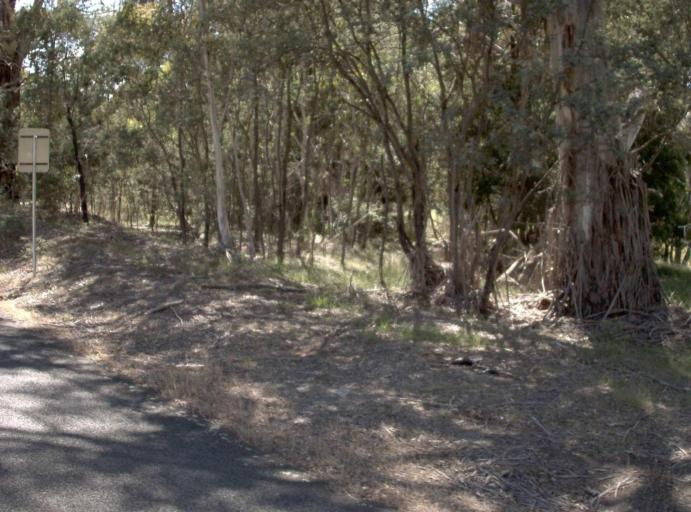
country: AU
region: New South Wales
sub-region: Bombala
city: Bombala
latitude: -37.0523
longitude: 148.8069
